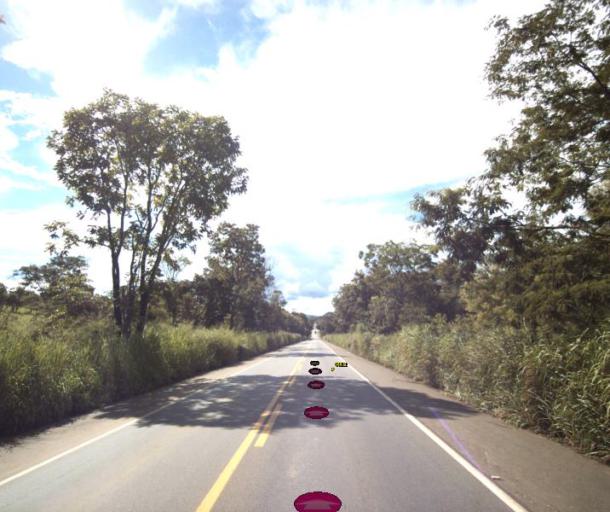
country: BR
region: Goias
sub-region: Jaragua
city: Jaragua
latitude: -15.7930
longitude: -49.3017
